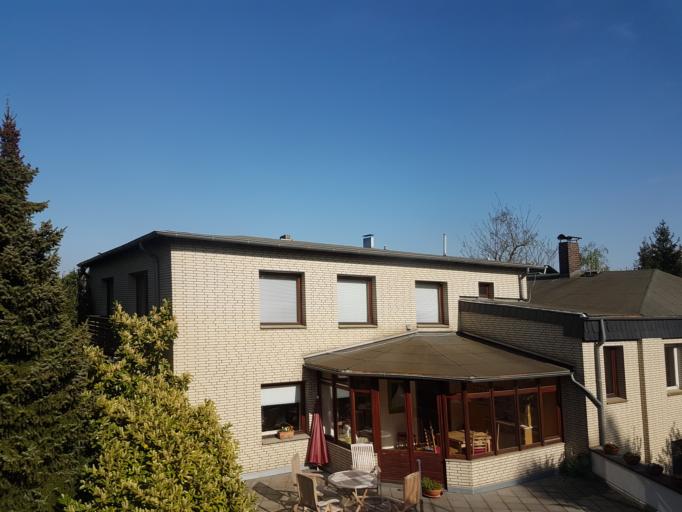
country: DE
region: Lower Saxony
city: Laatzen
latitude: 52.3481
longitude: 9.7730
